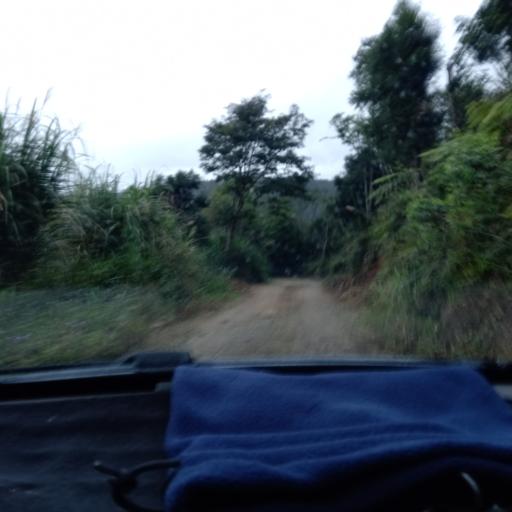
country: TW
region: Taiwan
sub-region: Yilan
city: Yilan
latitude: 24.8107
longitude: 121.6916
